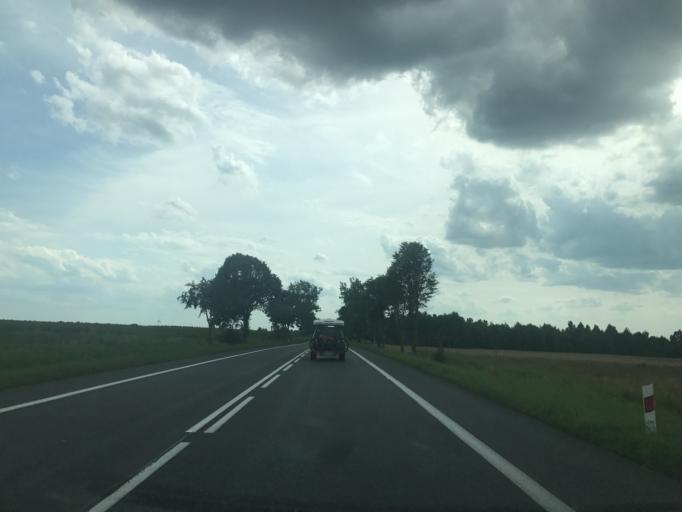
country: PL
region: Masovian Voivodeship
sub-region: Powiat mlawski
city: Wisniewo
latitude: 53.0178
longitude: 20.3338
